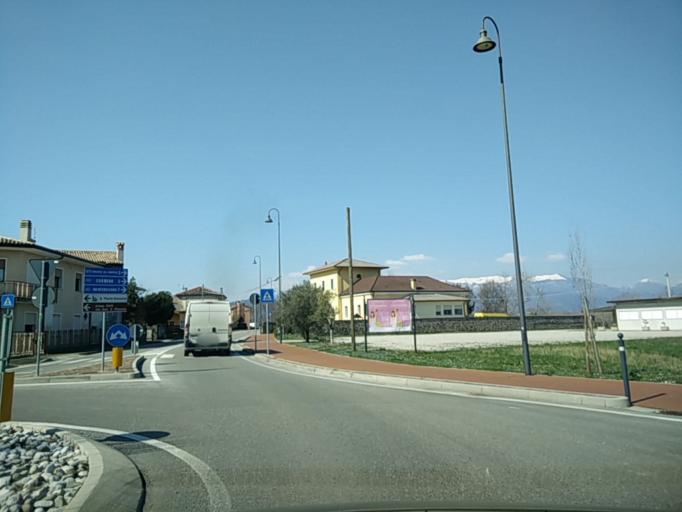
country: IT
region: Veneto
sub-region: Provincia di Treviso
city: Ciano
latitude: 45.8261
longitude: 12.0667
